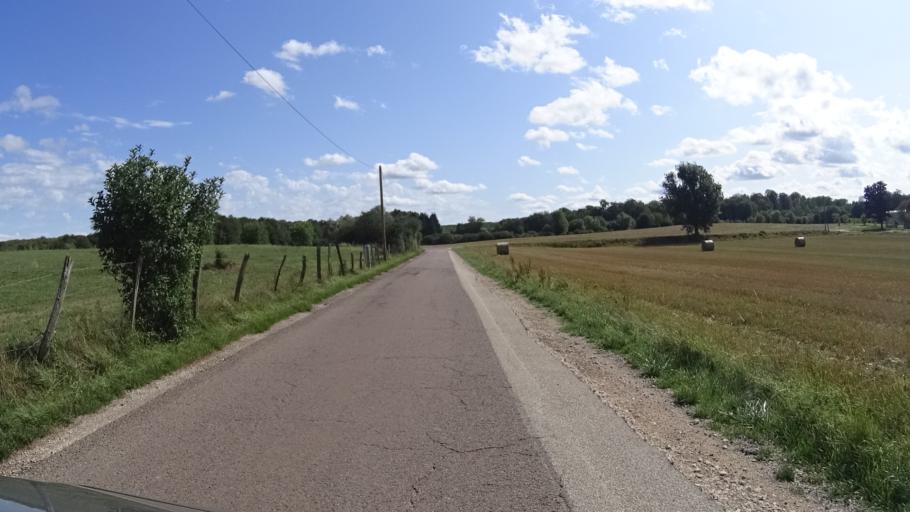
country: FR
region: Franche-Comte
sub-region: Departement du Doubs
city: Saone
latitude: 47.2088
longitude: 6.1104
